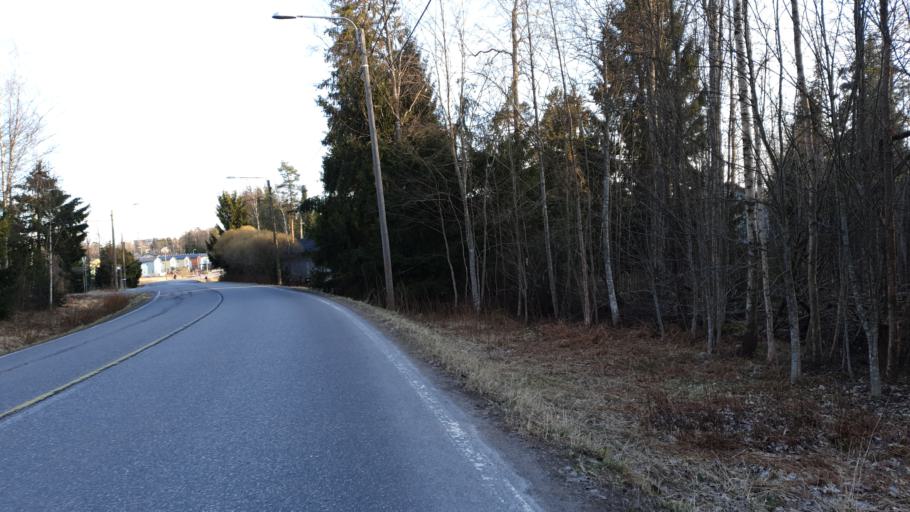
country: FI
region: Uusimaa
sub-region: Helsinki
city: Kilo
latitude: 60.3304
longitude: 24.8344
